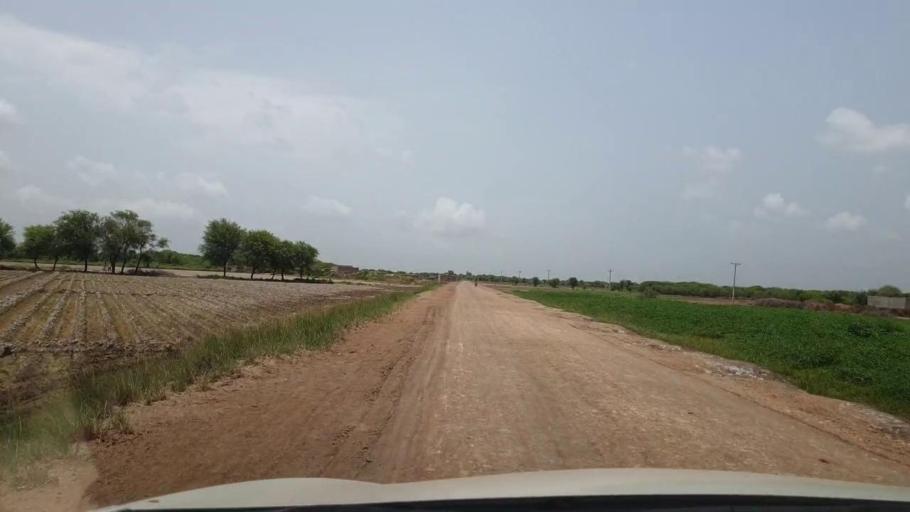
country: PK
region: Sindh
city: Chambar
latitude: 25.2010
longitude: 68.7613
